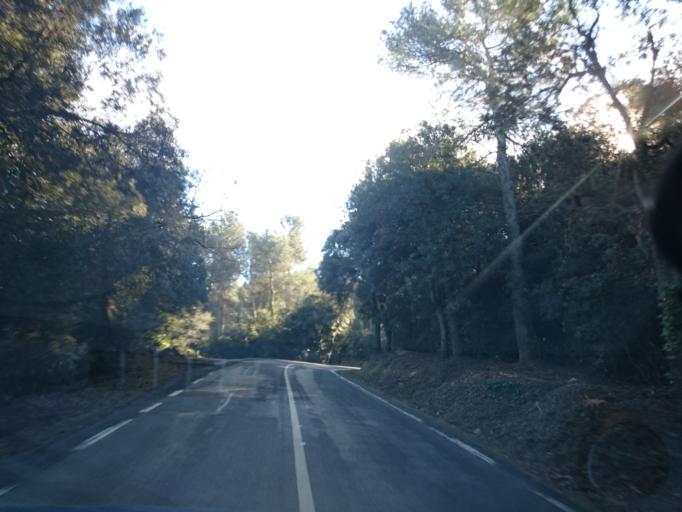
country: ES
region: Catalonia
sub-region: Provincia de Barcelona
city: Molins de Rei
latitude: 41.4289
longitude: 2.0574
